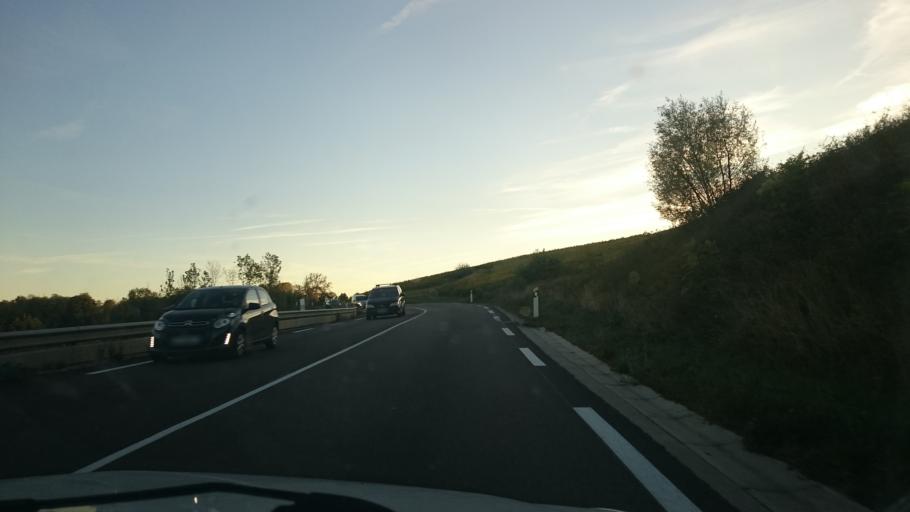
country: FR
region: Franche-Comte
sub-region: Departement du Jura
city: Poligny
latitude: 46.8791
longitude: 5.7180
